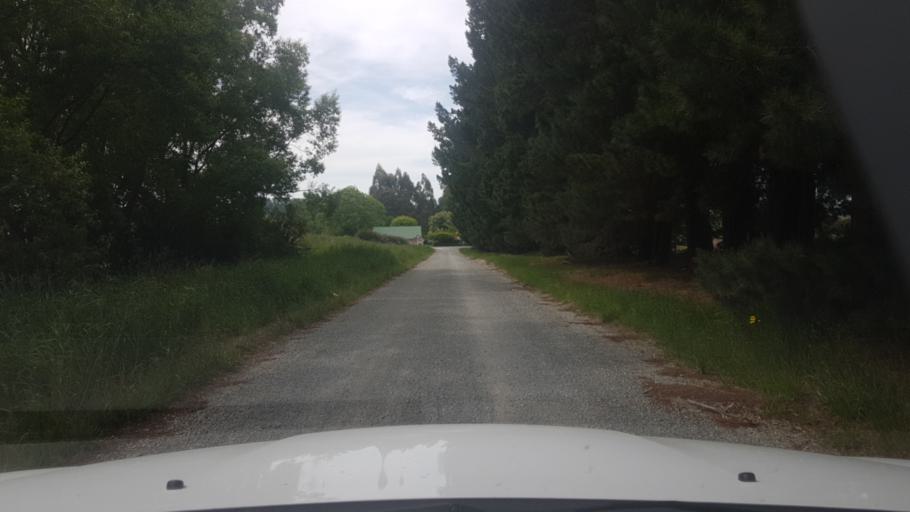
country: NZ
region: Canterbury
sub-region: Timaru District
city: Timaru
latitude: -44.4415
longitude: 171.1612
